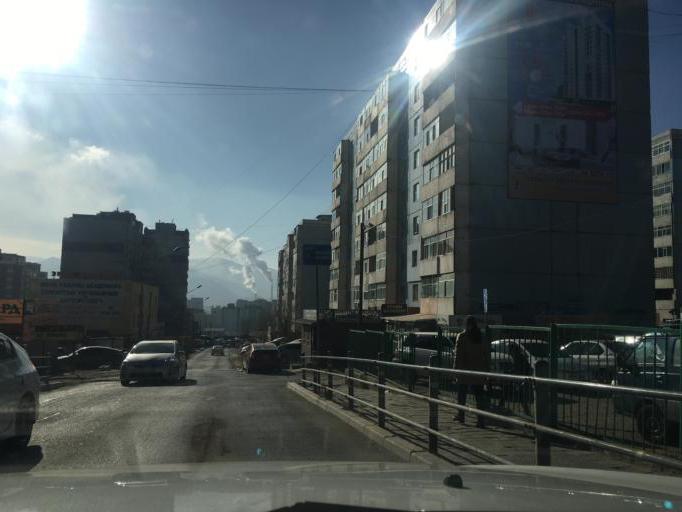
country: MN
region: Ulaanbaatar
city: Ulaanbaatar
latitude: 47.9218
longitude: 106.8661
